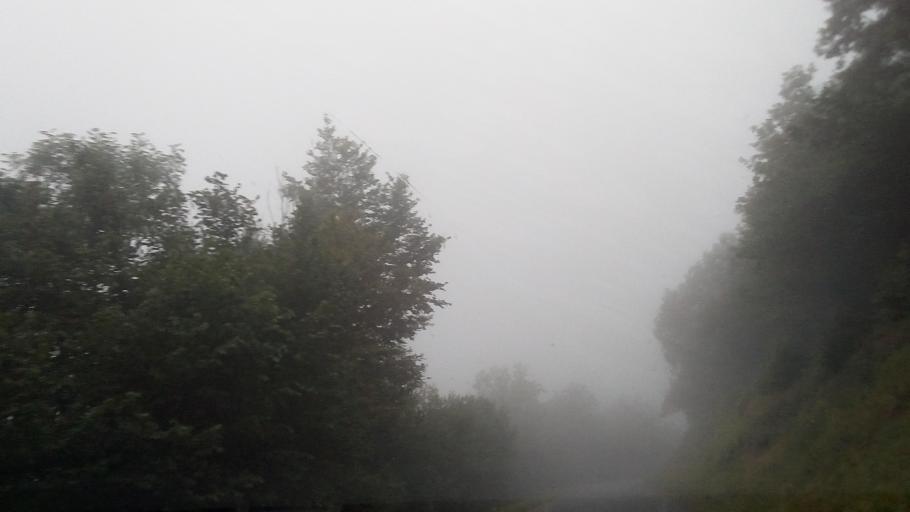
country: FR
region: Midi-Pyrenees
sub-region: Departement des Hautes-Pyrenees
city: Saint-Lary-Soulan
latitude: 42.8921
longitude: 0.3229
